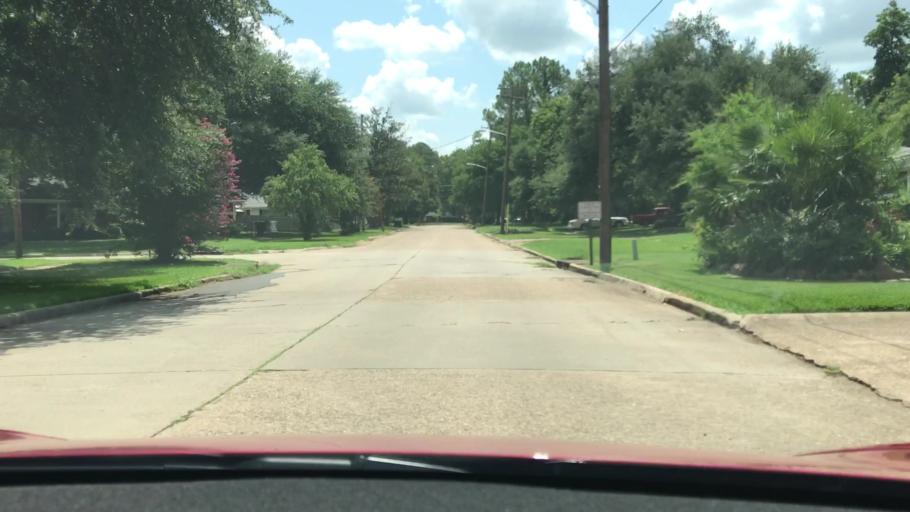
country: US
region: Louisiana
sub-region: Bossier Parish
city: Bossier City
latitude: 32.4576
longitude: -93.7312
